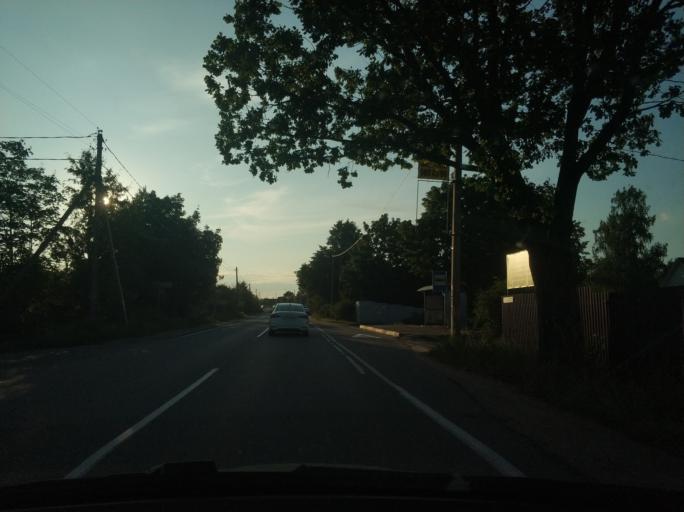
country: RU
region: Leningrad
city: Borisova Griva
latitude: 60.0834
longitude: 31.0316
